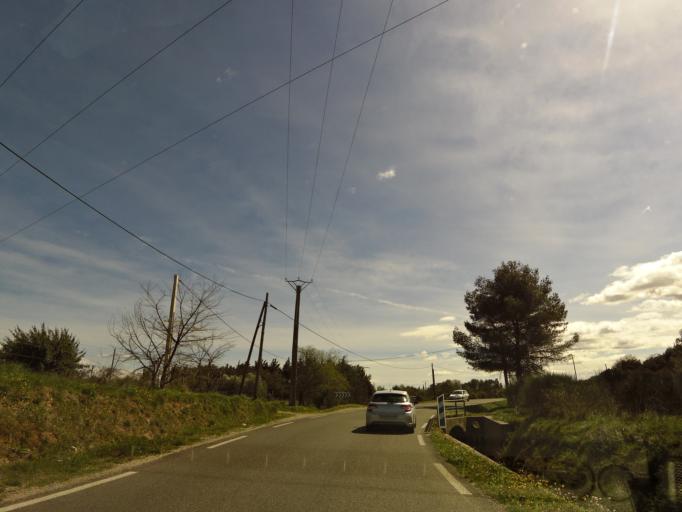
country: FR
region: Languedoc-Roussillon
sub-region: Departement du Gard
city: Bernis
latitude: 43.7776
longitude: 4.2817
